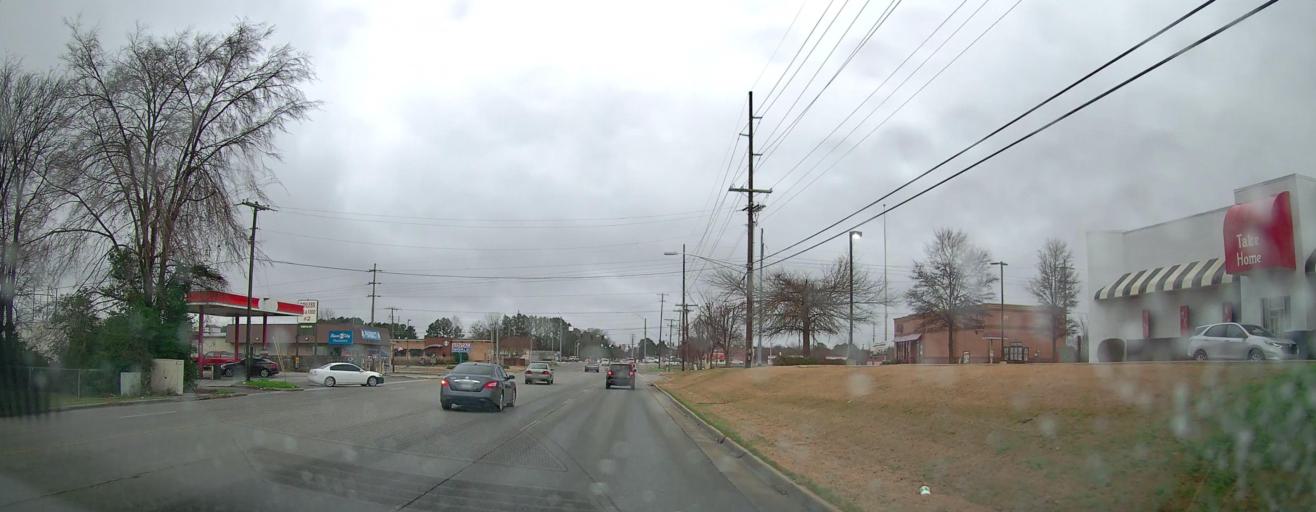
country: US
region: Alabama
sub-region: Morgan County
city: Flint City
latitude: 34.5577
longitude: -87.0001
